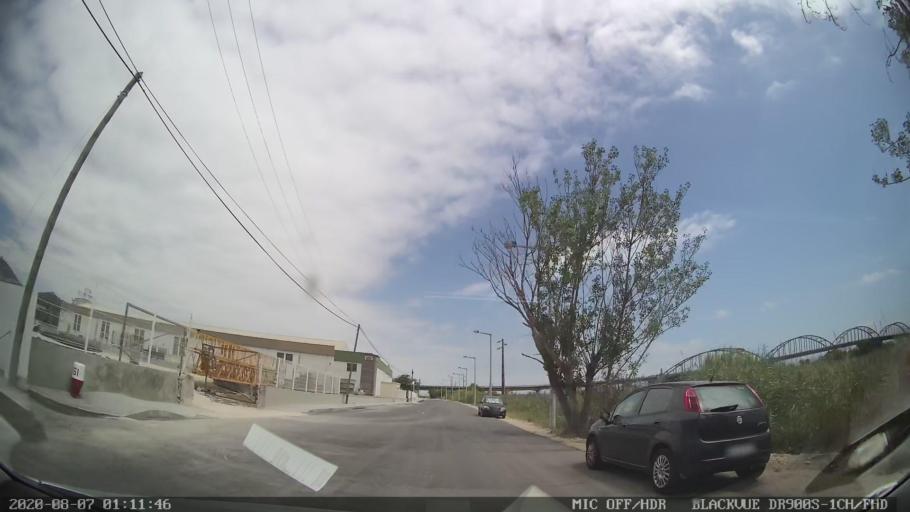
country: PT
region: Lisbon
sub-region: Vila Franca de Xira
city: Vila Franca de Xira
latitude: 38.9569
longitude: -8.9843
